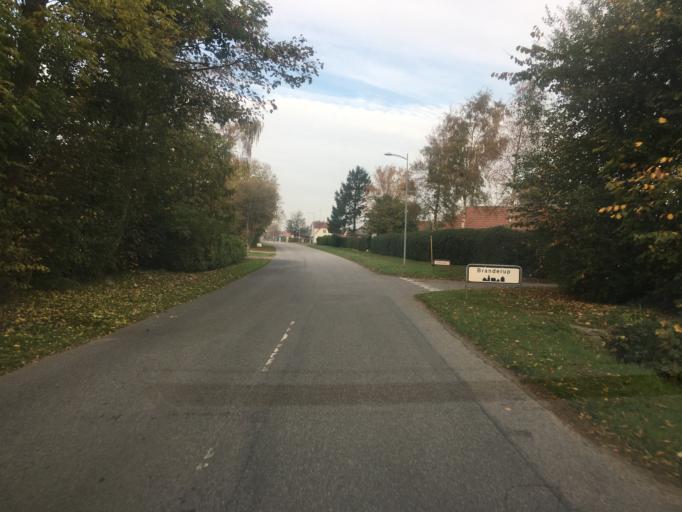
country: DK
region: South Denmark
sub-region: Tonder Kommune
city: Toftlund
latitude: 55.1181
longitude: 9.0727
